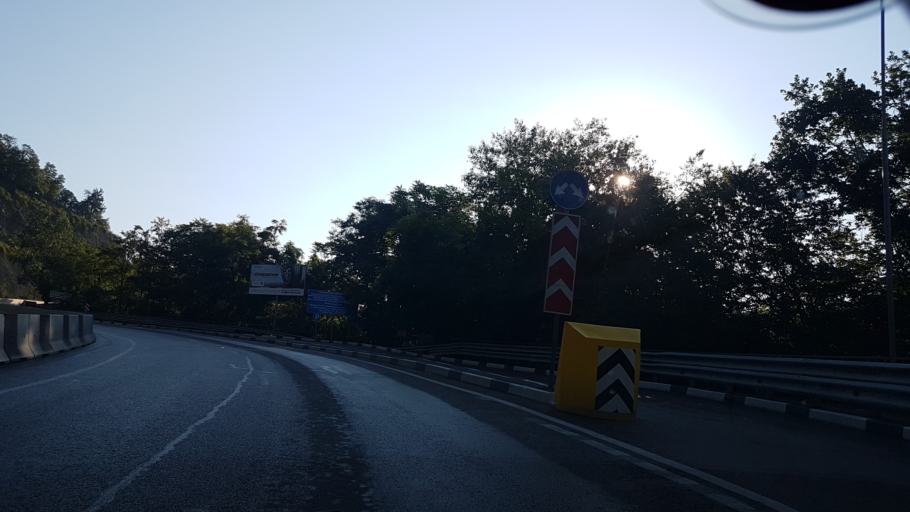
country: RU
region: Krasnodarskiy
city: Dagomys
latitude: 43.6408
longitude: 39.6987
